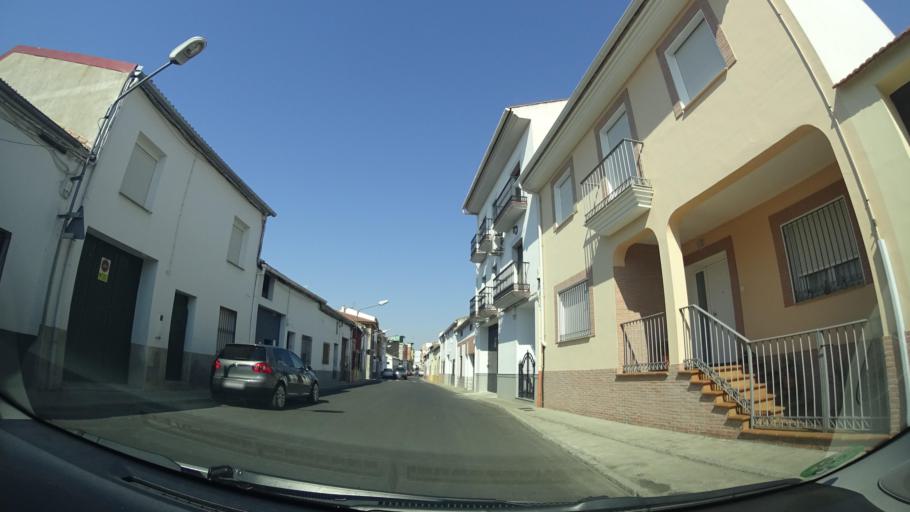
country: ES
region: Extremadura
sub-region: Provincia de Caceres
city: Miajadas
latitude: 39.1481
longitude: -5.9108
